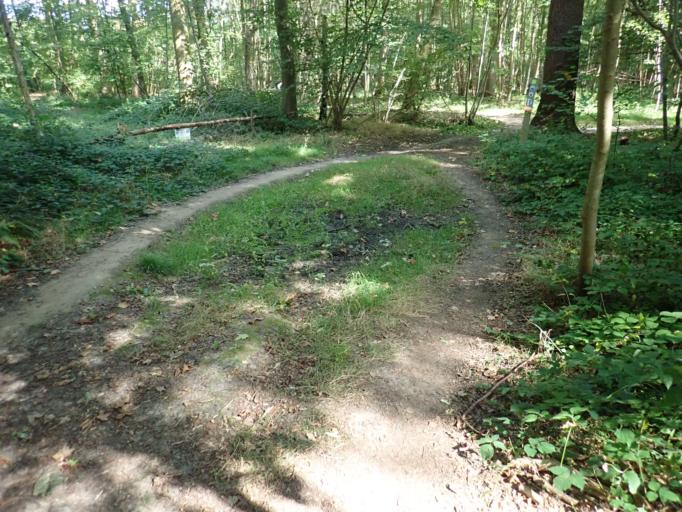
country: BE
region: Flanders
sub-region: Provincie Antwerpen
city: Boechout
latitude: 51.1436
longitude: 4.4955
